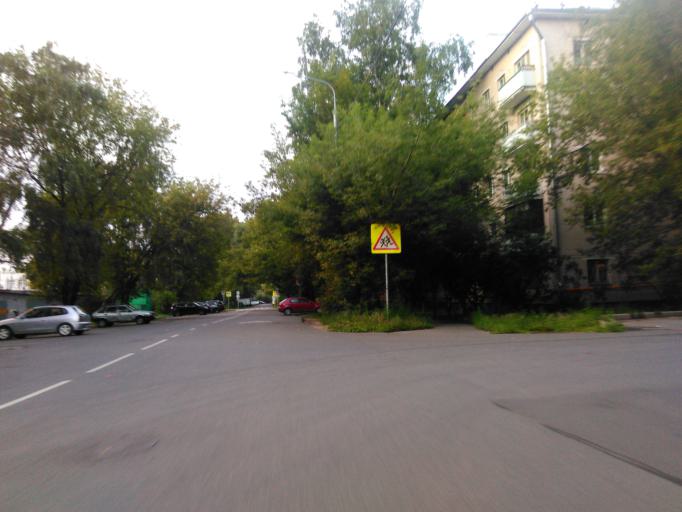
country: RU
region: Moscow
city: Yaroslavskiy
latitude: 55.8760
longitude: 37.7141
